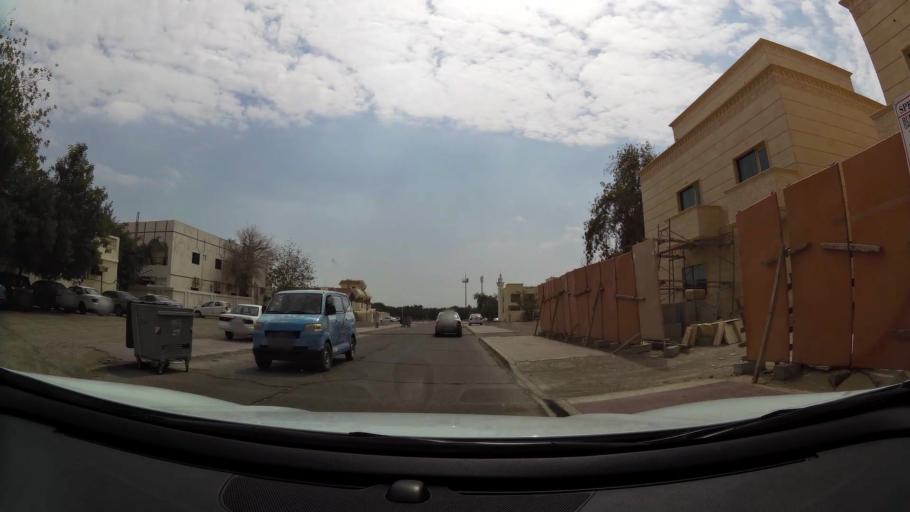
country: AE
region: Abu Dhabi
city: Al Ain
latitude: 24.2127
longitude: 55.7897
